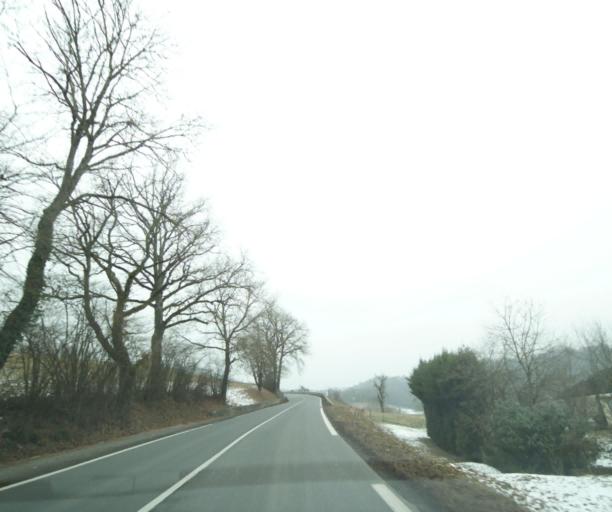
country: FR
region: Rhone-Alpes
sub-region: Departement de la Haute-Savoie
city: Arthaz-Pont-Notre-Dame
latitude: 46.1560
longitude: 6.2471
